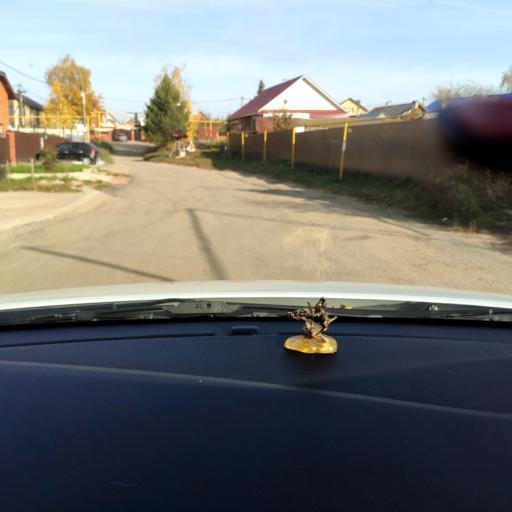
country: RU
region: Tatarstan
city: Vysokaya Gora
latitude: 55.7970
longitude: 49.2690
